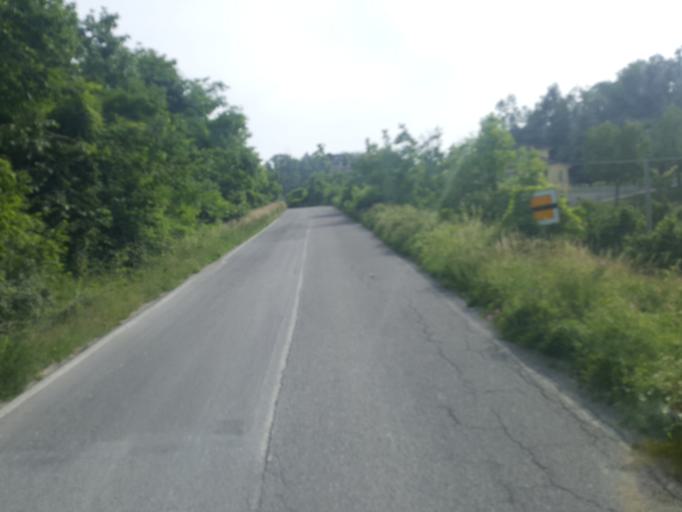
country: IT
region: Emilia-Romagna
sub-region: Provincia di Piacenza
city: Ponte dell'Olio
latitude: 44.8763
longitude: 9.6254
